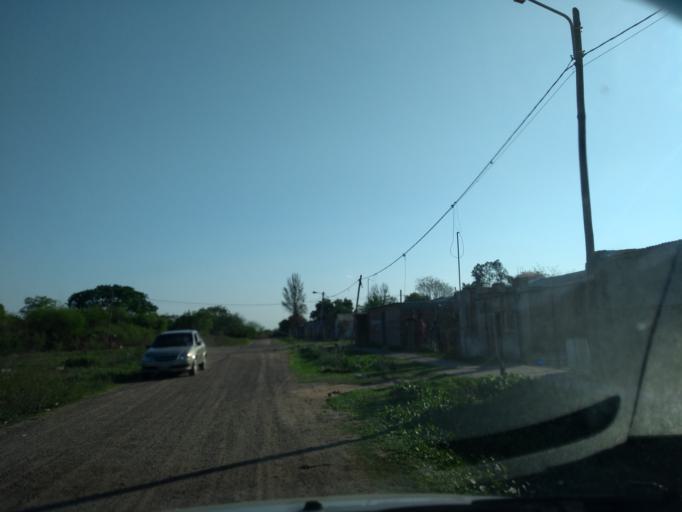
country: AR
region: Chaco
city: Fontana
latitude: -27.4154
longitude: -59.0586
